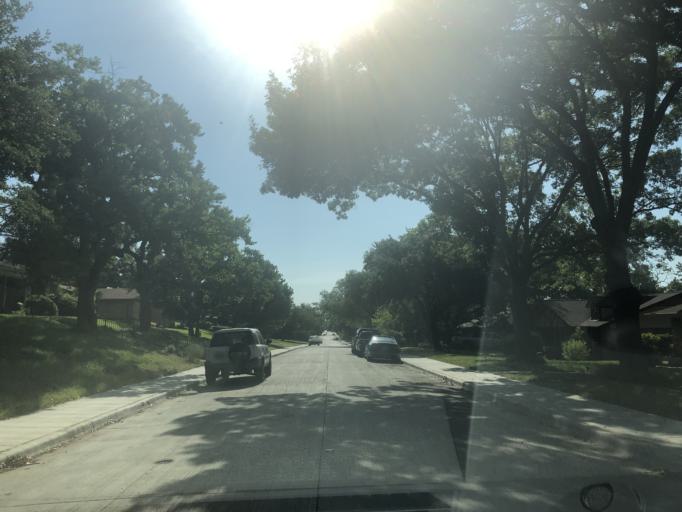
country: US
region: Texas
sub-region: Dallas County
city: Grand Prairie
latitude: 32.7540
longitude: -97.0257
